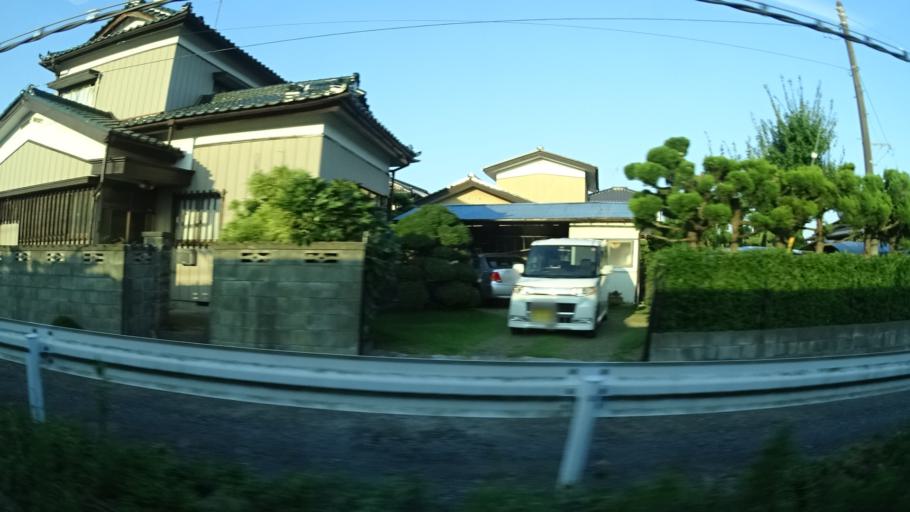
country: JP
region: Ibaraki
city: Ishioka
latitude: 36.2423
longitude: 140.2882
